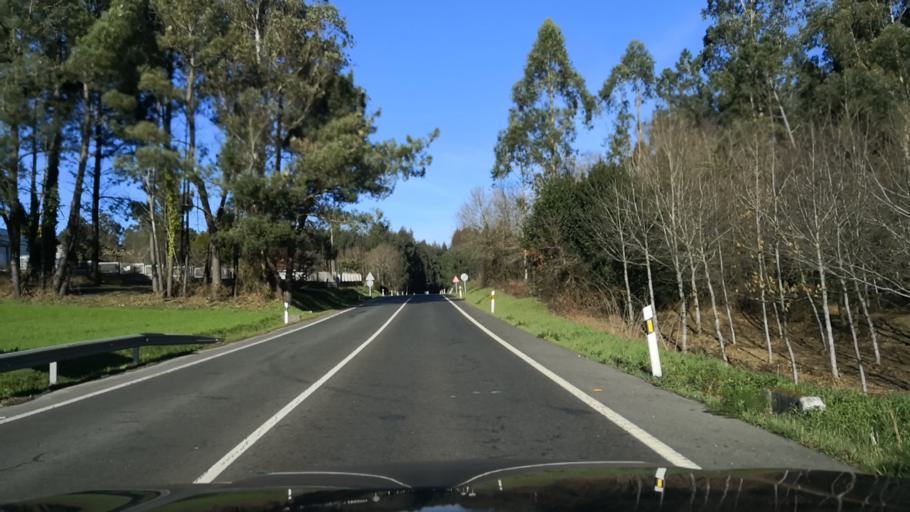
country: ES
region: Galicia
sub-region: Provincia da Coruna
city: Ribeira
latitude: 42.7049
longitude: -8.4235
